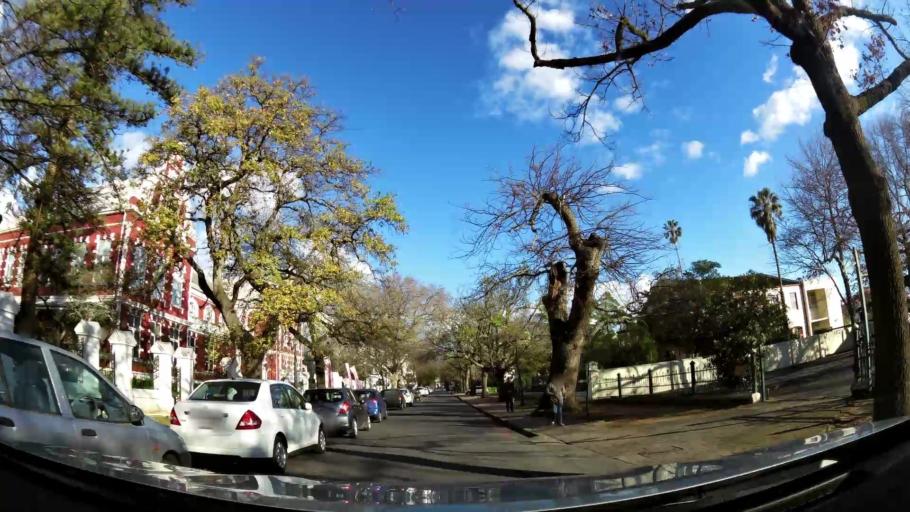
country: ZA
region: Western Cape
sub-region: Cape Winelands District Municipality
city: Stellenbosch
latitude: -33.9349
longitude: 18.8625
